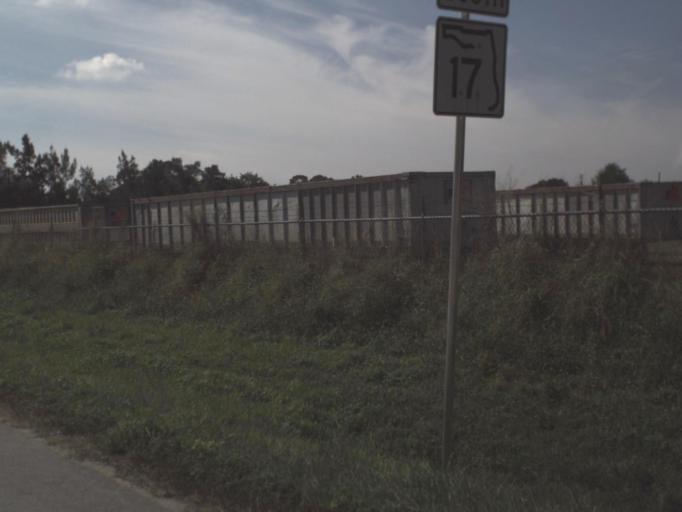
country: US
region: Florida
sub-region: Highlands County
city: Sebring
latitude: 27.5559
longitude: -81.4532
